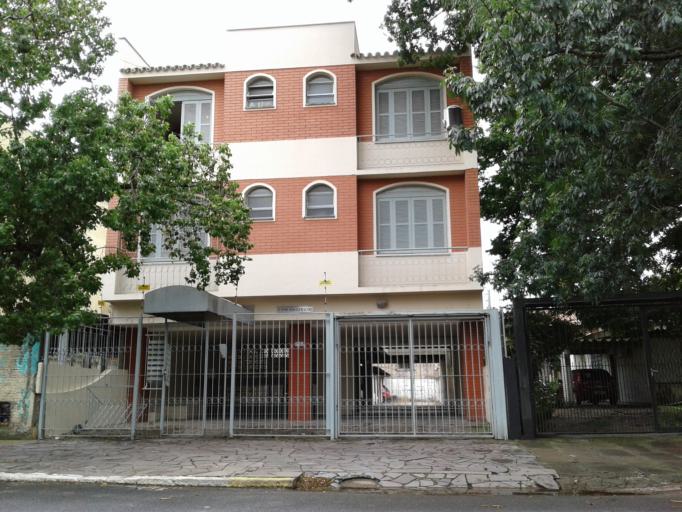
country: BR
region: Rio Grande do Sul
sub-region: Porto Alegre
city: Porto Alegre
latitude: -30.0451
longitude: -51.2235
